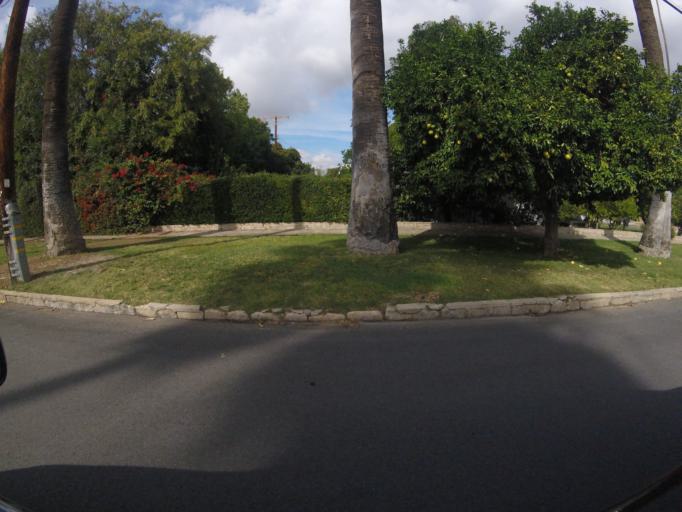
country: US
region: California
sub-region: San Bernardino County
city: Redlands
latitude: 34.0481
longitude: -117.1673
